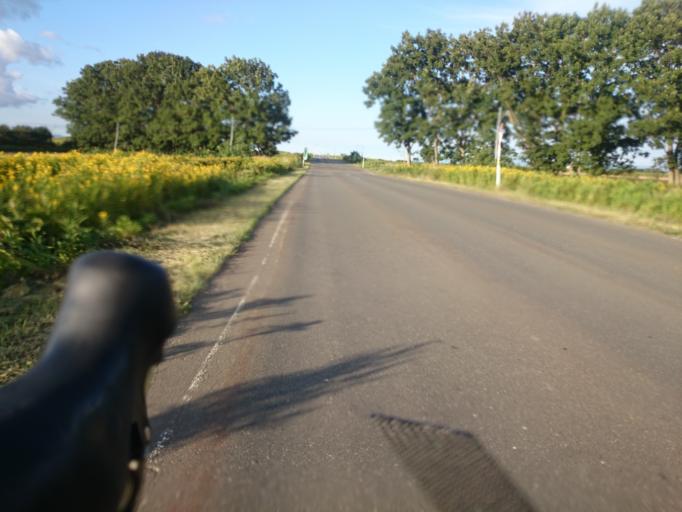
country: JP
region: Hokkaido
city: Tobetsu
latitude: 43.1846
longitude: 141.5597
